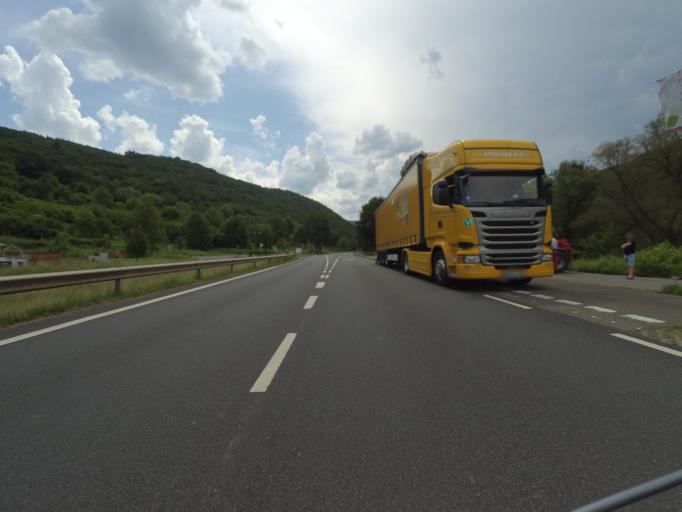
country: DE
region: Rheinland-Pfalz
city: Burgen
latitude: 50.2044
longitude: 7.3818
